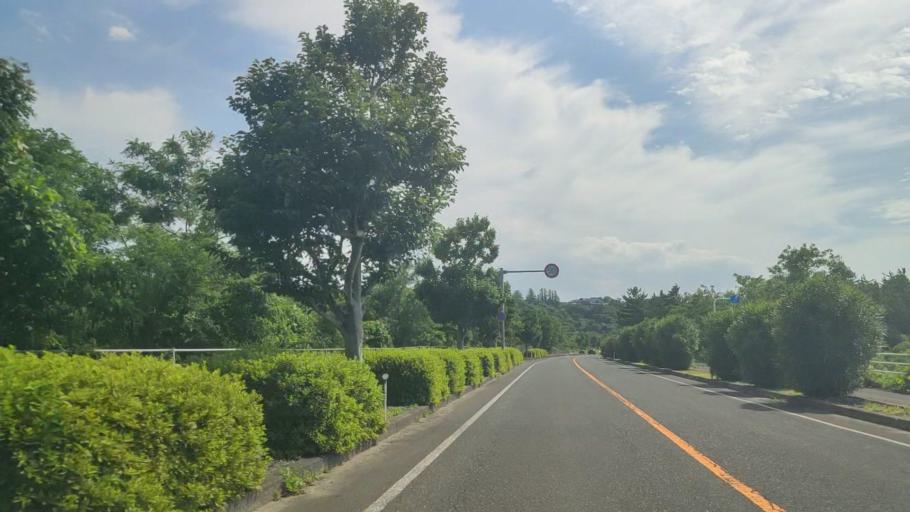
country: JP
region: Tottori
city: Tottori
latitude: 35.5371
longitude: 134.2348
